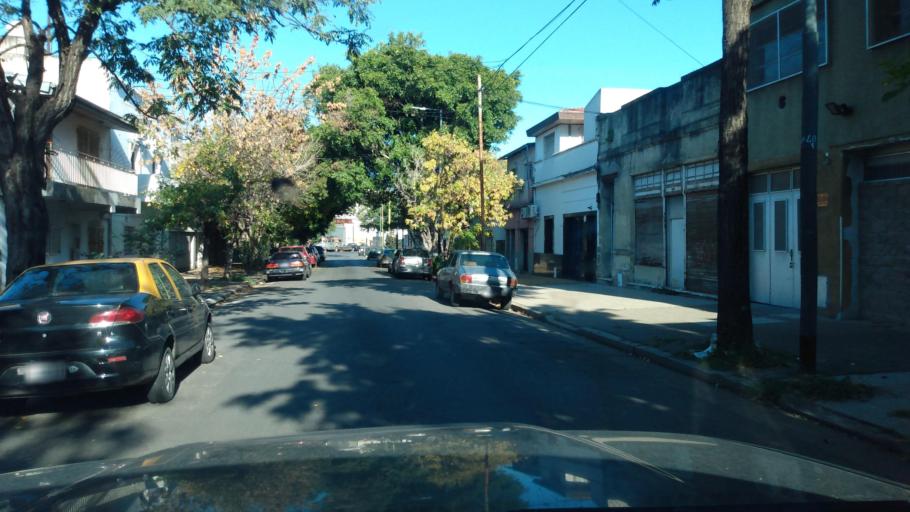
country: AR
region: Buenos Aires F.D.
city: Villa Santa Rita
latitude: -34.5950
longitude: -58.4692
